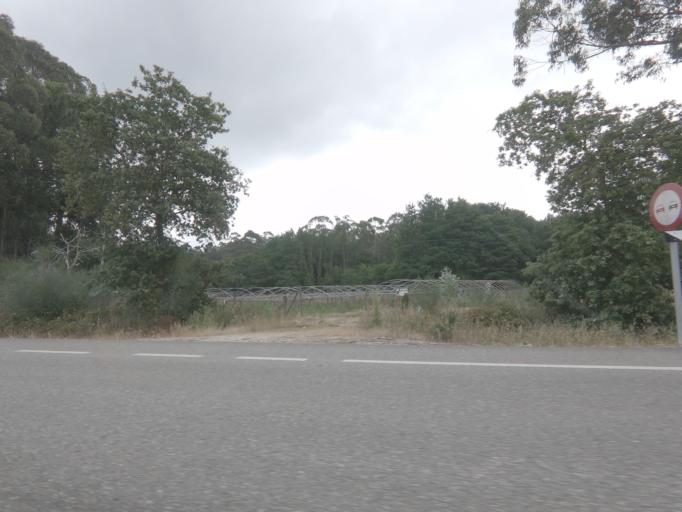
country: ES
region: Galicia
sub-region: Provincia de Pontevedra
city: O Rosal
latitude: 41.9365
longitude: -8.7911
